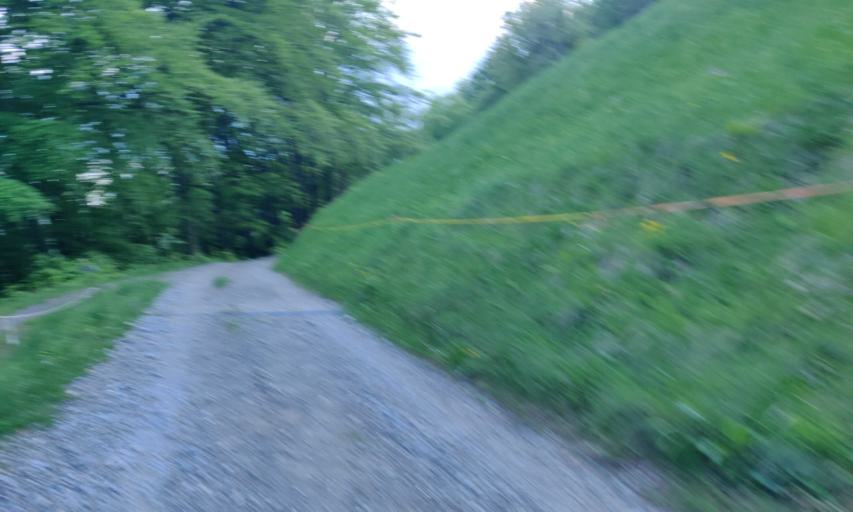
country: CH
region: Saint Gallen
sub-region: Wahlkreis Sarganserland
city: Sargans
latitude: 47.0742
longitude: 9.4543
